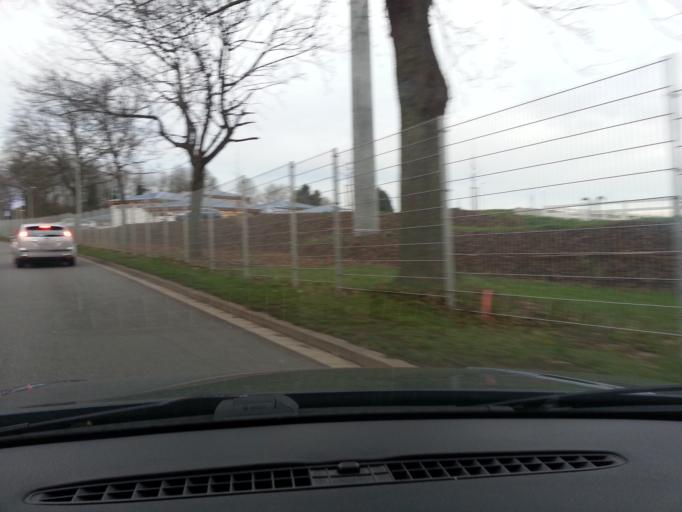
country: DE
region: Saarland
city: Neunkirchen
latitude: 49.3292
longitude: 7.1861
